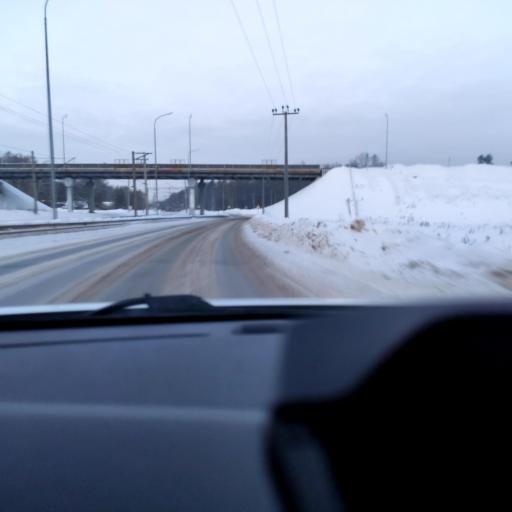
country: RU
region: Tatarstan
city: Vysokaya Gora
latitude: 55.9440
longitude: 49.3350
